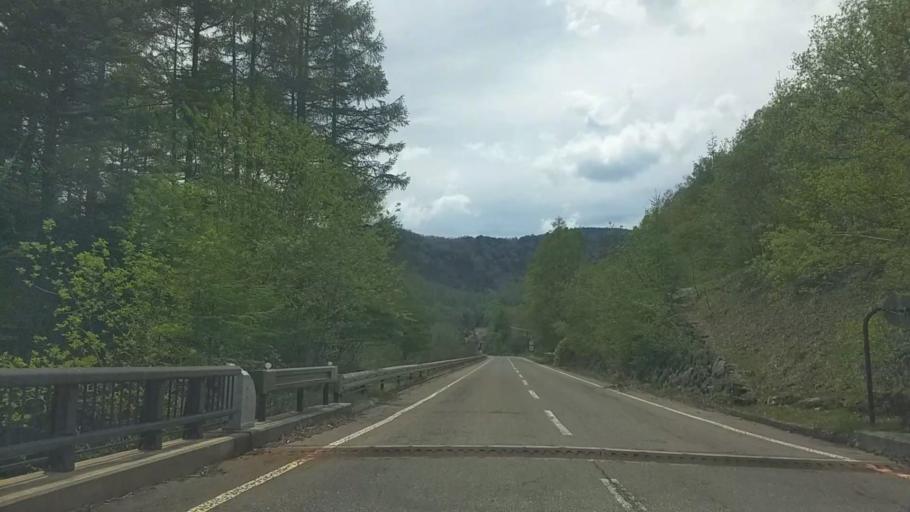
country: JP
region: Nagano
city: Saku
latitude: 36.0740
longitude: 138.3819
